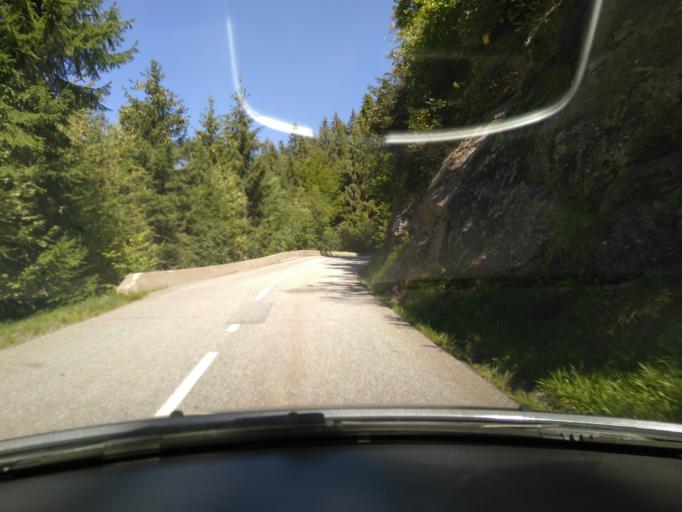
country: FR
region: Rhone-Alpes
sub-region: Departement de la Savoie
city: Ugine
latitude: 45.7945
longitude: 6.4901
